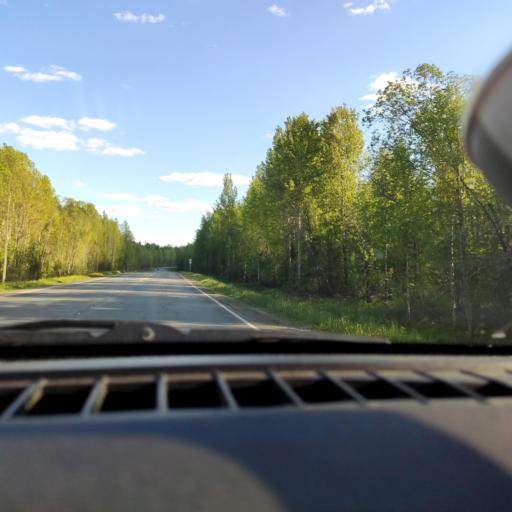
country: RU
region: Perm
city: Polazna
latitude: 58.2689
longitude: 56.1673
